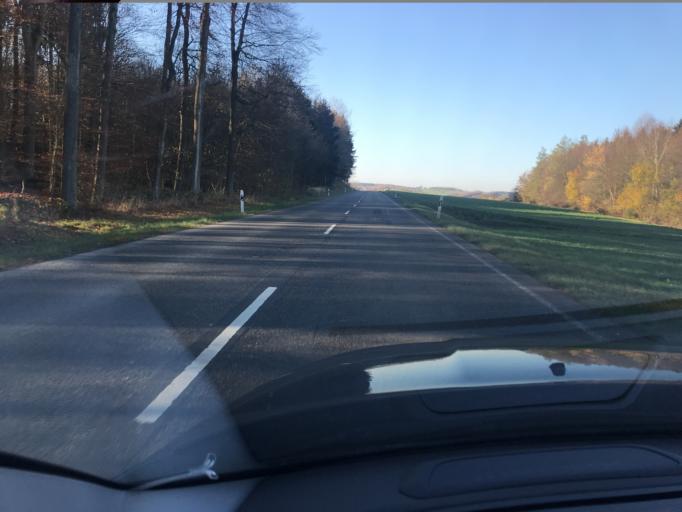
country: DE
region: Rheinland-Pfalz
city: Nomborn
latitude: 50.4396
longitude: 7.9322
